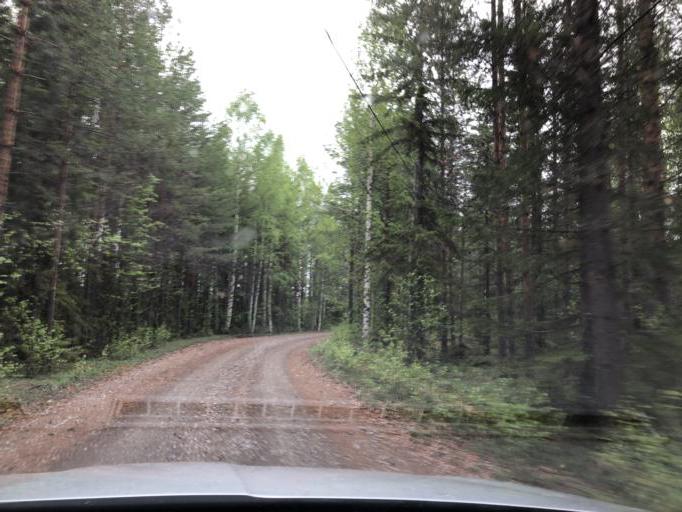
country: SE
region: Norrbotten
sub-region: Pitea Kommun
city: Roknas
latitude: 65.3958
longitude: 21.2656
